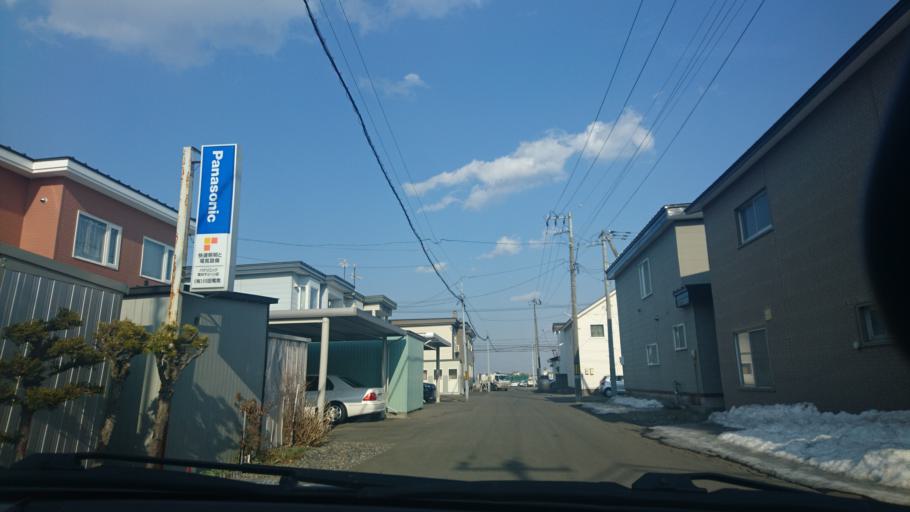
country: JP
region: Hokkaido
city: Obihiro
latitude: 42.9191
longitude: 143.1501
